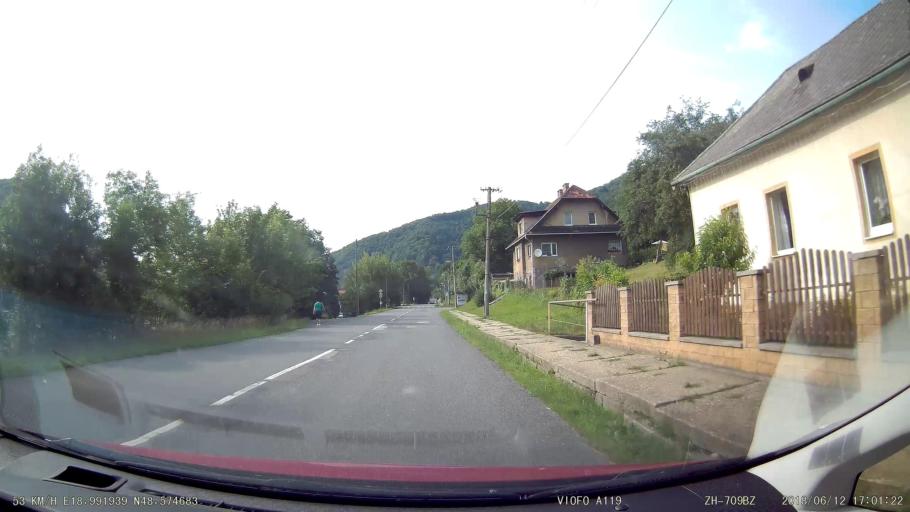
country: SK
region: Banskobystricky
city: Ziar nad Hronom
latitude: 48.5748
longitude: 18.9919
